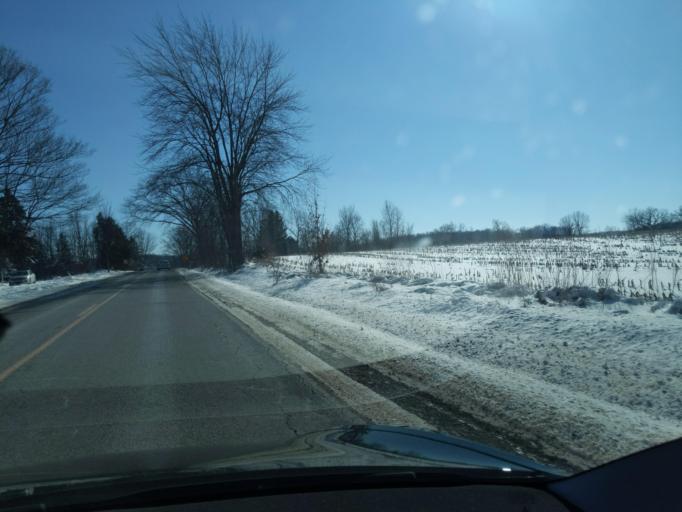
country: US
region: Michigan
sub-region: Livingston County
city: Fowlerville
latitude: 42.5489
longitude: -84.0697
